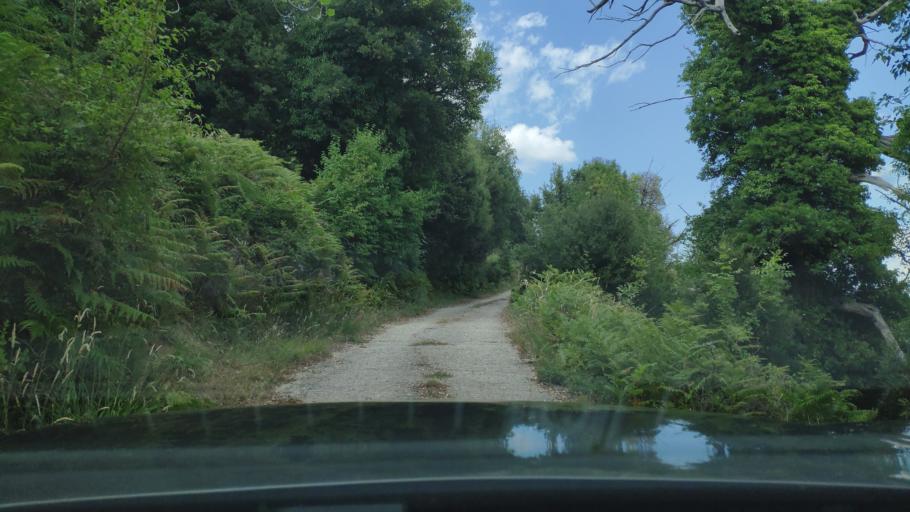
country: GR
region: Epirus
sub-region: Nomos Artas
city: Agios Dimitrios
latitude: 39.3198
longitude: 20.9995
